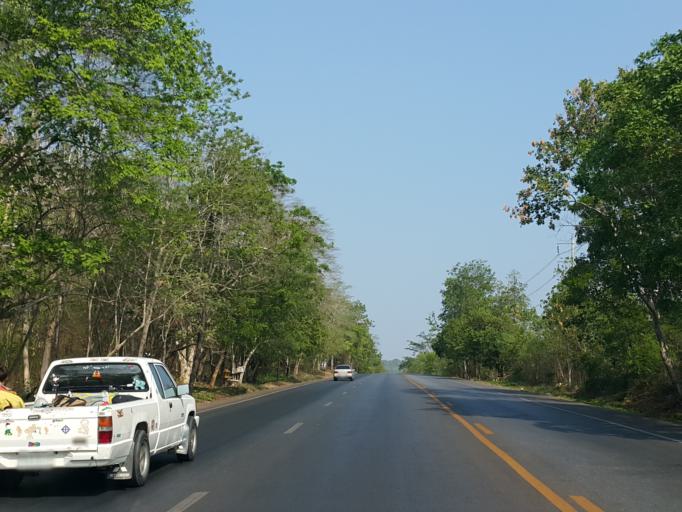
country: TH
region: Kanchanaburi
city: Sai Yok
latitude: 14.1061
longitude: 99.2193
